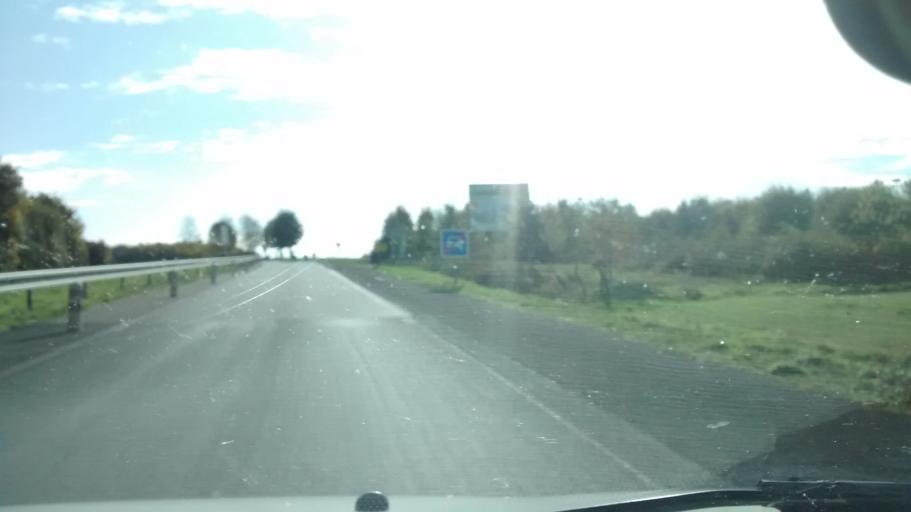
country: FR
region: Pays de la Loire
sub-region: Departement de Maine-et-Loire
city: Pouance
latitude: 47.7492
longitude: -1.1581
